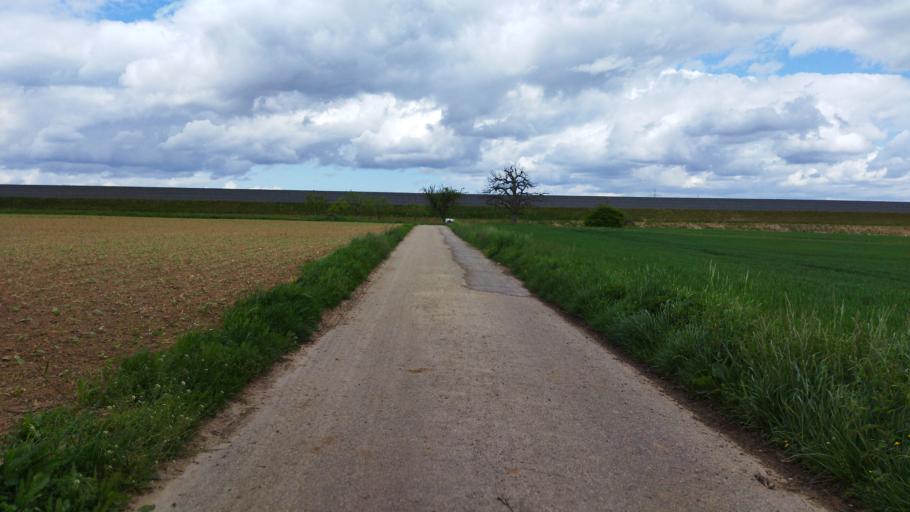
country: DE
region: Baden-Wuerttemberg
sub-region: Regierungsbezirk Stuttgart
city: Leingarten
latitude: 49.1860
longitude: 9.1195
